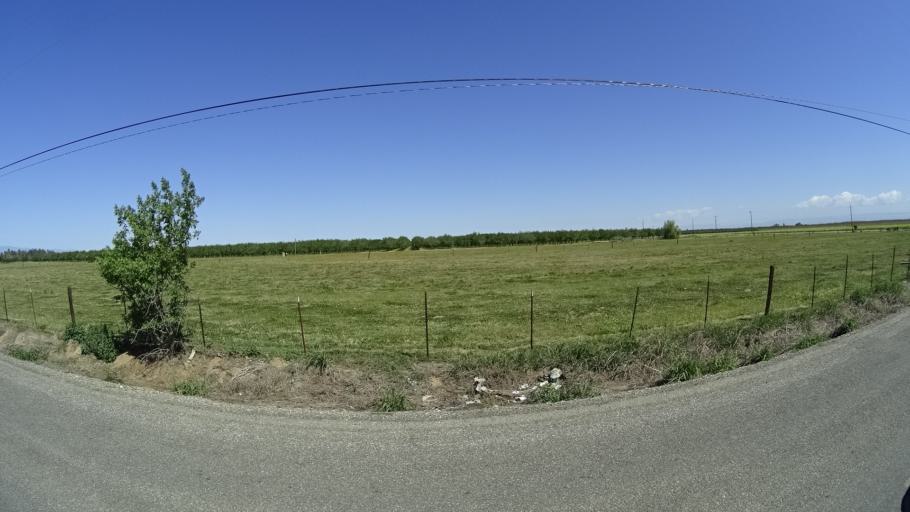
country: US
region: California
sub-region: Glenn County
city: Orland
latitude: 39.6964
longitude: -122.1655
